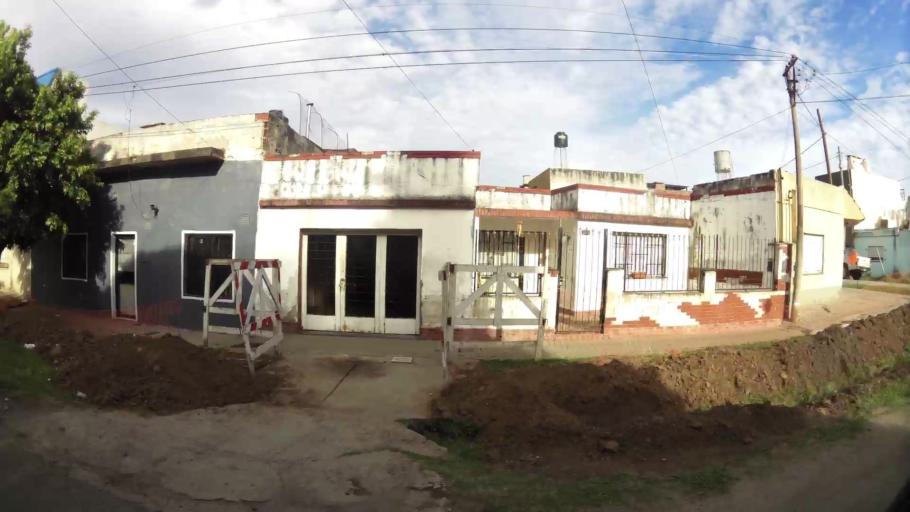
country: AR
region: Santa Fe
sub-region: Departamento de Rosario
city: Rosario
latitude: -32.9789
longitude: -60.6763
